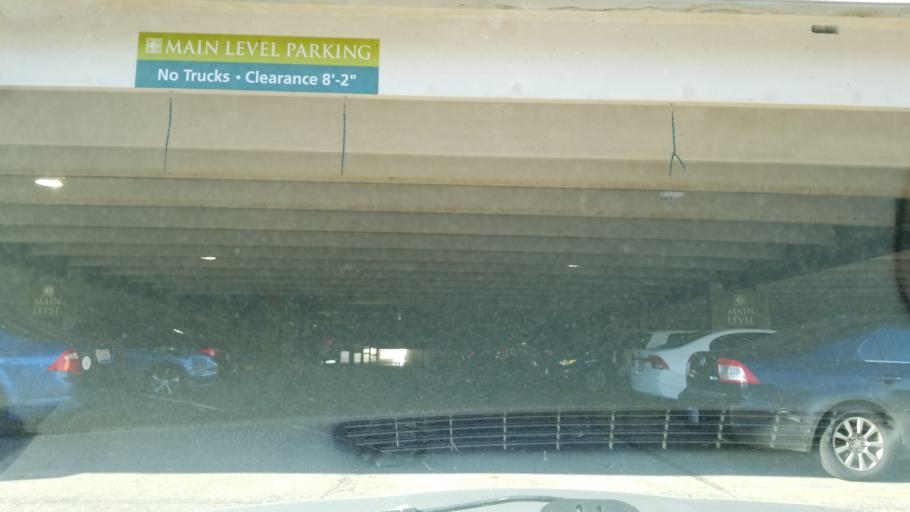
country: US
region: Ohio
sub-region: Cuyahoga County
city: University Heights
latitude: 41.4997
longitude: -81.5330
